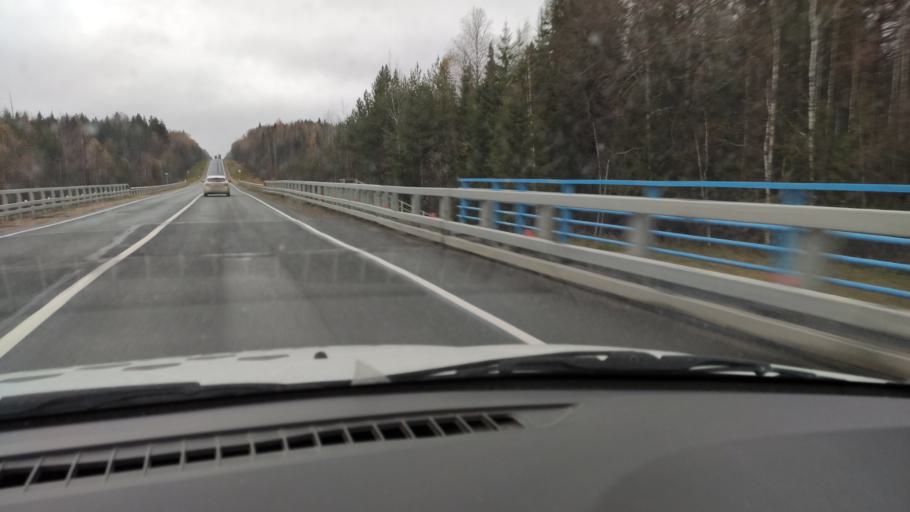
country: RU
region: Kirov
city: Chernaya Kholunitsa
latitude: 58.8591
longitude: 51.6899
